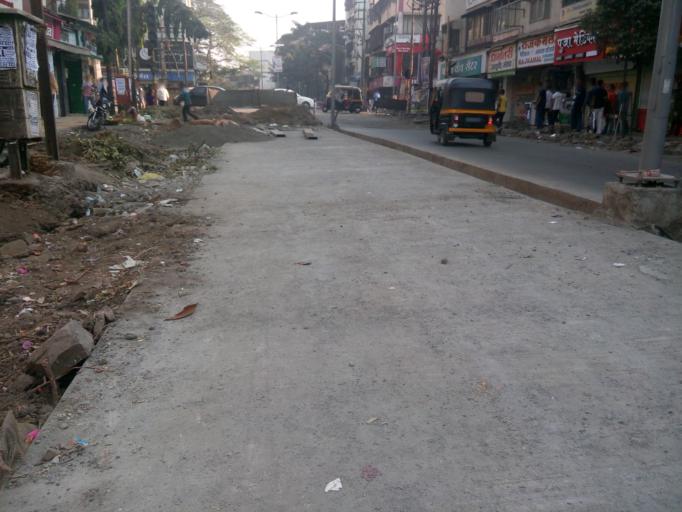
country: IN
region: Maharashtra
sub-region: Thane
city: Dombivli
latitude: 19.2147
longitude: 73.0909
